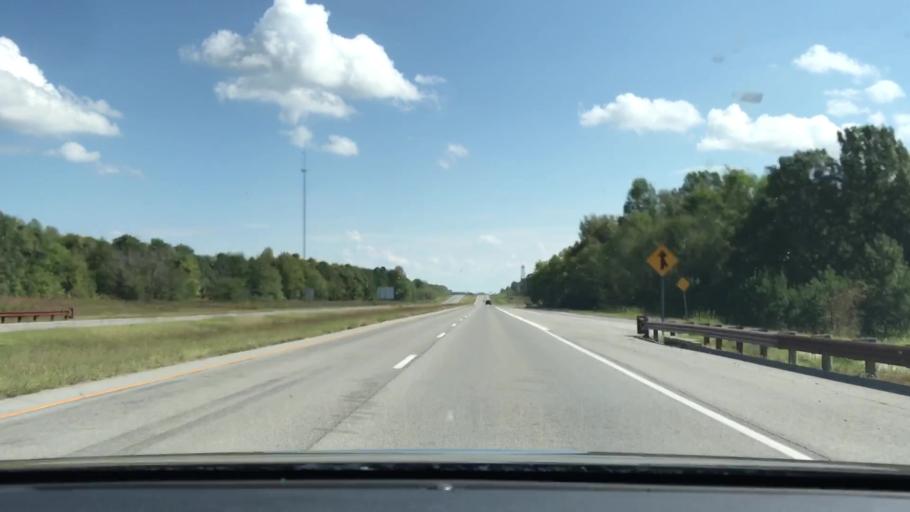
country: US
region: Kentucky
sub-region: Trigg County
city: Cadiz
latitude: 36.7794
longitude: -88.0654
